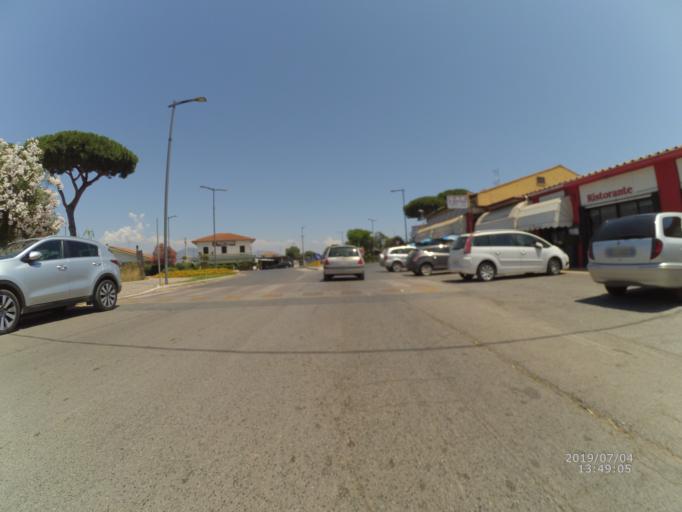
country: IT
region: Latium
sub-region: Provincia di Latina
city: San Felice Circeo
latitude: 41.2852
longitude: 13.1112
